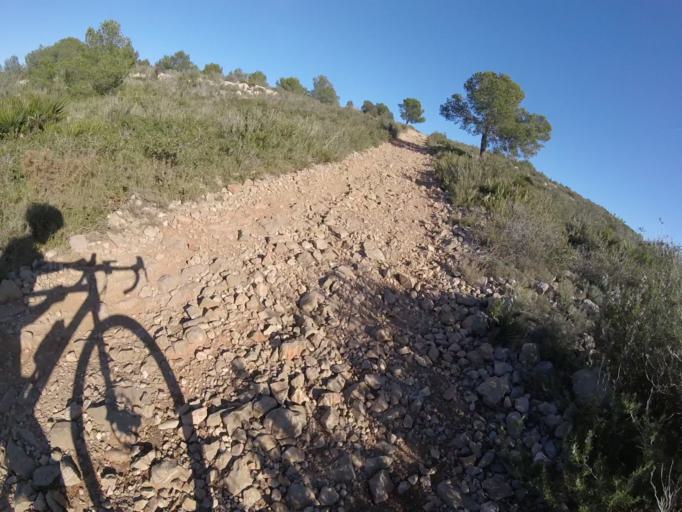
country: ES
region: Valencia
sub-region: Provincia de Castello
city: Orpesa/Oropesa del Mar
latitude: 40.0976
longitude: 0.1078
